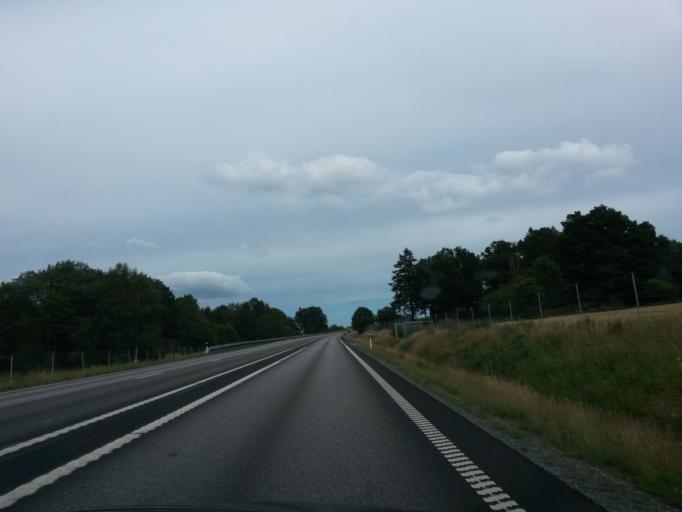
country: SE
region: Vaestra Goetaland
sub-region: Marks Kommun
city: Kinna
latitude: 57.4785
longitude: 12.6332
